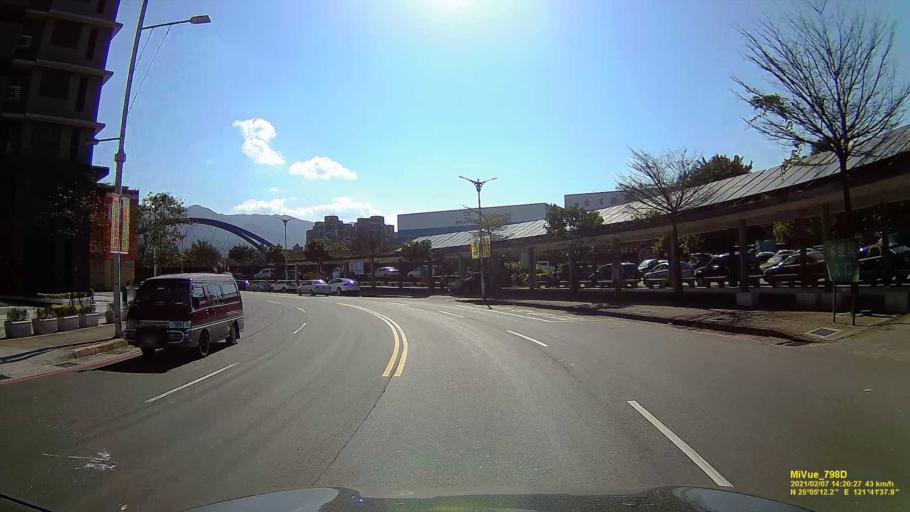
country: TW
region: Taiwan
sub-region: Keelung
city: Keelung
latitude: 25.0865
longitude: 121.6936
